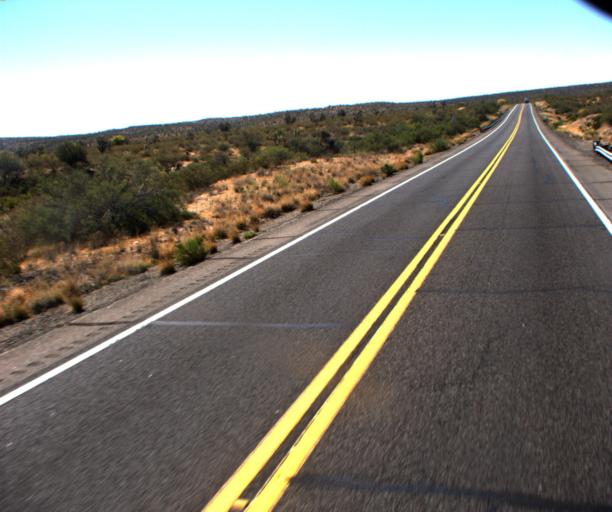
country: US
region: Arizona
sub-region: Yavapai County
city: Congress
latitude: 34.2129
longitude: -113.0664
